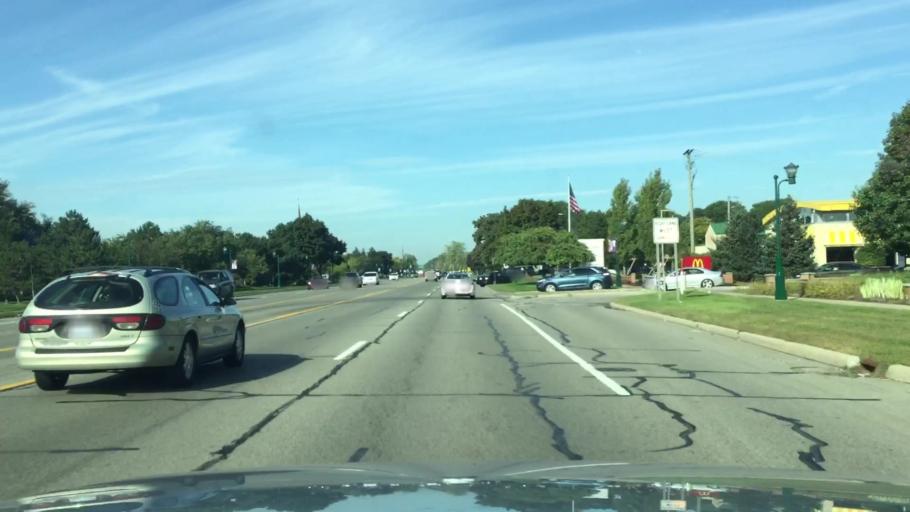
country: US
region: Michigan
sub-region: Wayne County
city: Canton
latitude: 42.3221
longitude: -83.4812
